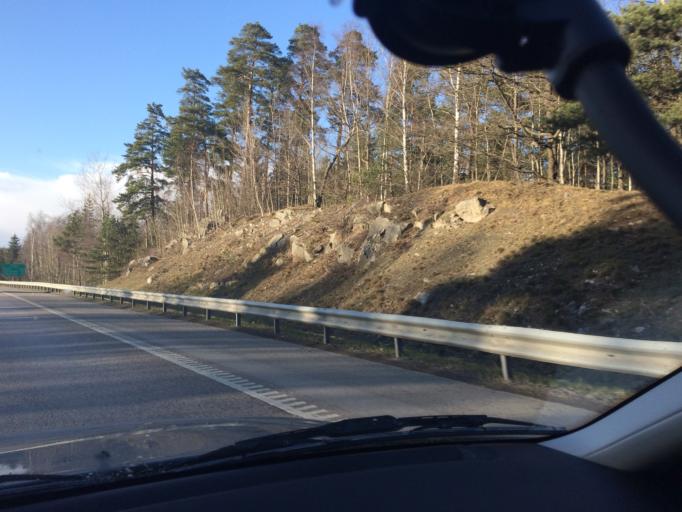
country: SE
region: Stockholm
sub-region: Jarfalla Kommun
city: Jakobsberg
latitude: 59.4274
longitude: 17.8501
